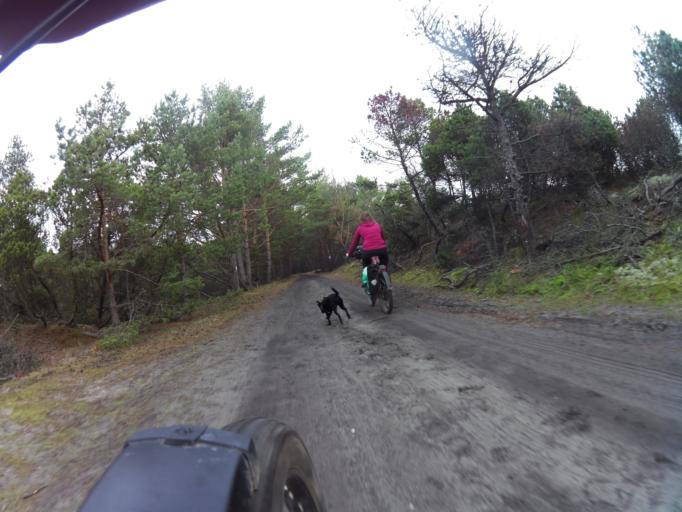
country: PL
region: Pomeranian Voivodeship
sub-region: Powiat pucki
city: Hel
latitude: 54.6198
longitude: 18.8197
